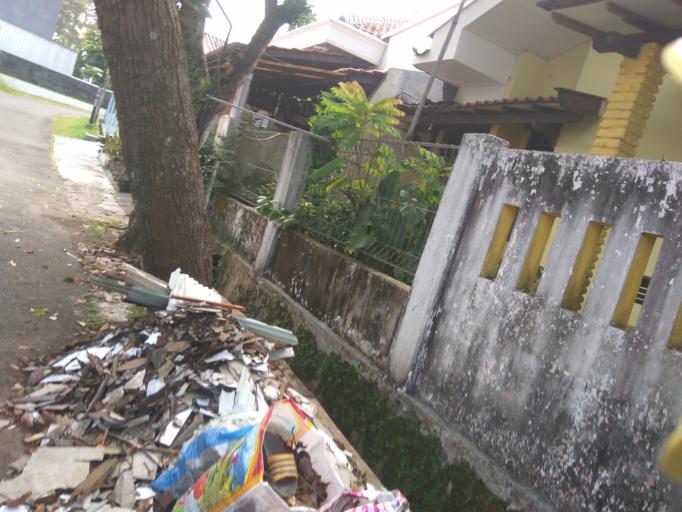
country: ID
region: Central Java
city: Semarang
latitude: -7.0455
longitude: 110.4172
